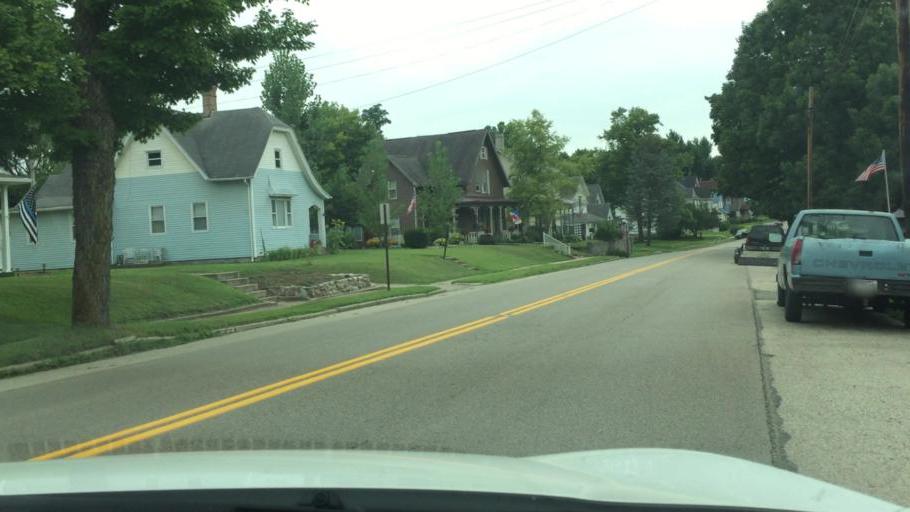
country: US
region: Ohio
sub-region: Champaign County
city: Mechanicsburg
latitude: 40.0748
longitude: -83.5516
